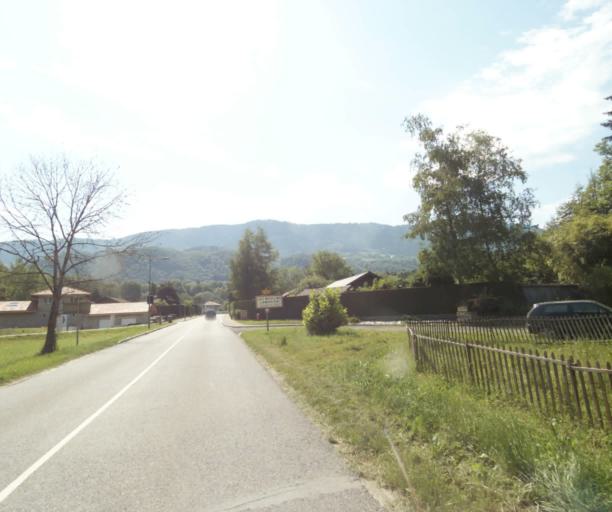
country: FR
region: Rhone-Alpes
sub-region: Departement de la Haute-Savoie
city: Armoy
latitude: 46.3346
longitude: 6.5000
